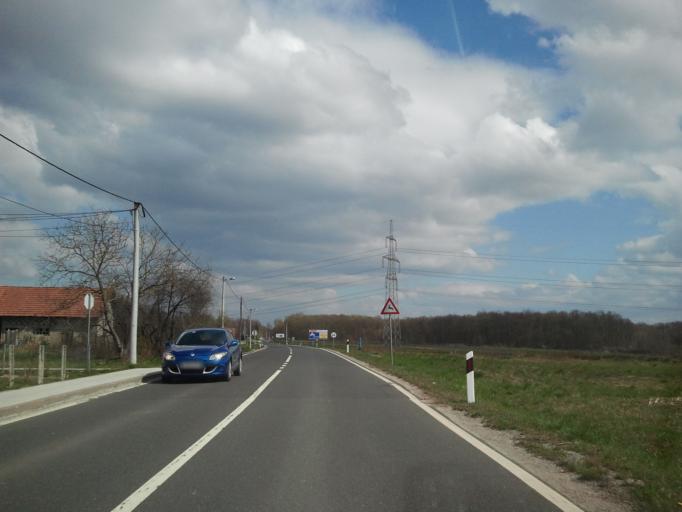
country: HR
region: Grad Zagreb
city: Horvati
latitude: 45.7129
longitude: 15.7782
